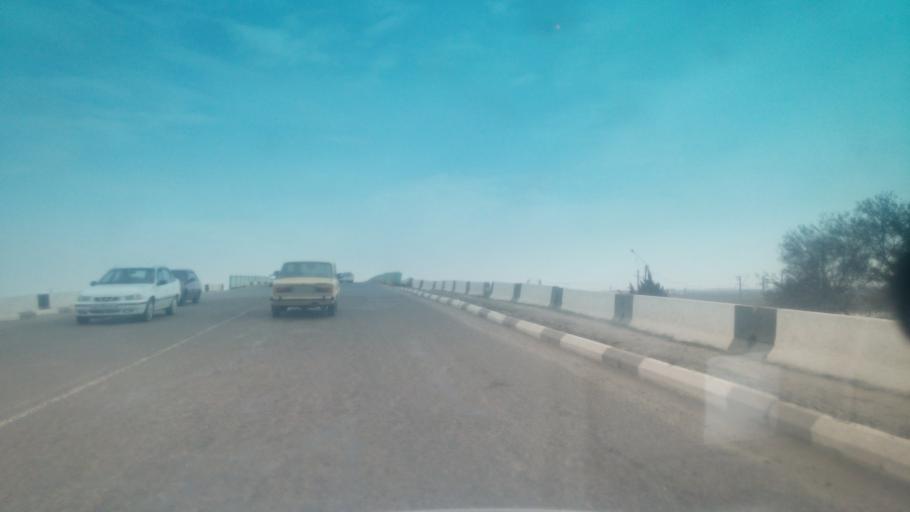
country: UZ
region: Sirdaryo
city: Guliston
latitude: 40.4734
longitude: 68.7680
